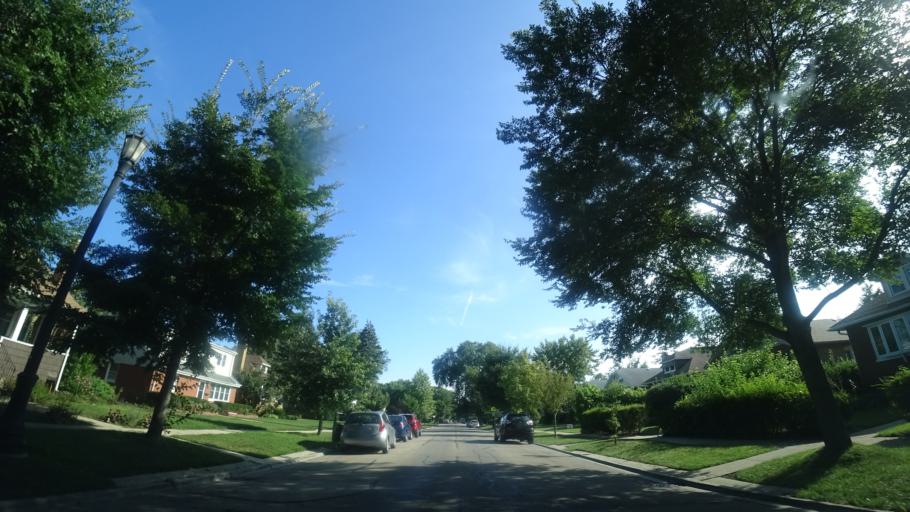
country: US
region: Illinois
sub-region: Cook County
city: Evanston
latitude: 42.0438
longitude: -87.7069
